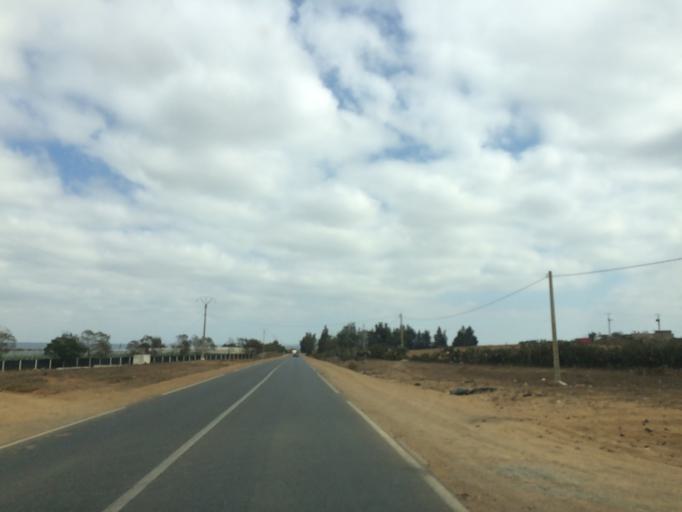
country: MA
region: Gharb-Chrarda-Beni Hssen
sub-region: Kenitra Province
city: Lalla Mimouna
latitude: 34.8412
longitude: -6.1728
